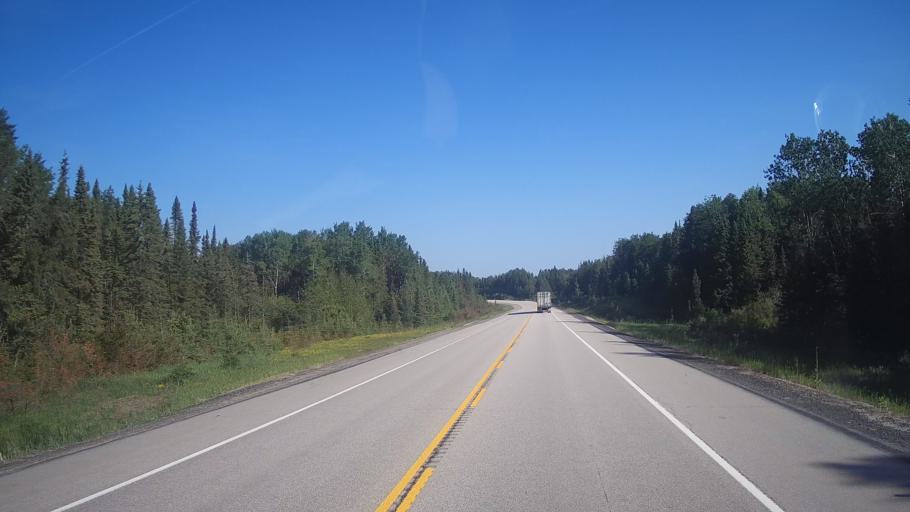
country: CA
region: Ontario
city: Dryden
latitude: 49.5799
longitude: -92.2622
